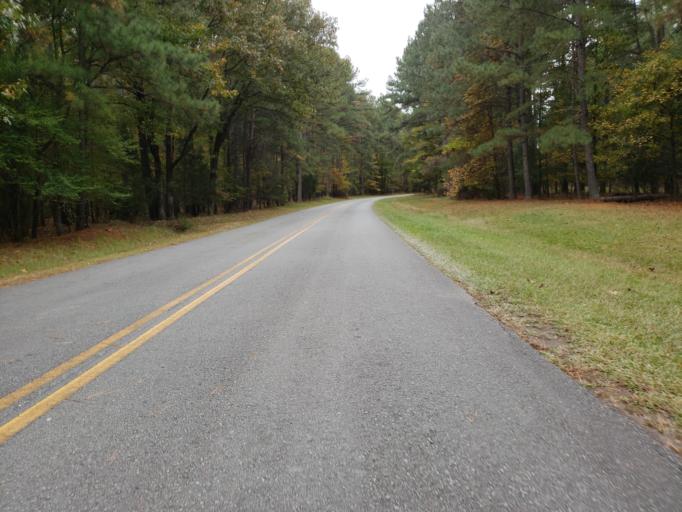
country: US
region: North Carolina
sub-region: Chatham County
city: Fearrington Village
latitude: 35.7594
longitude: -79.0443
